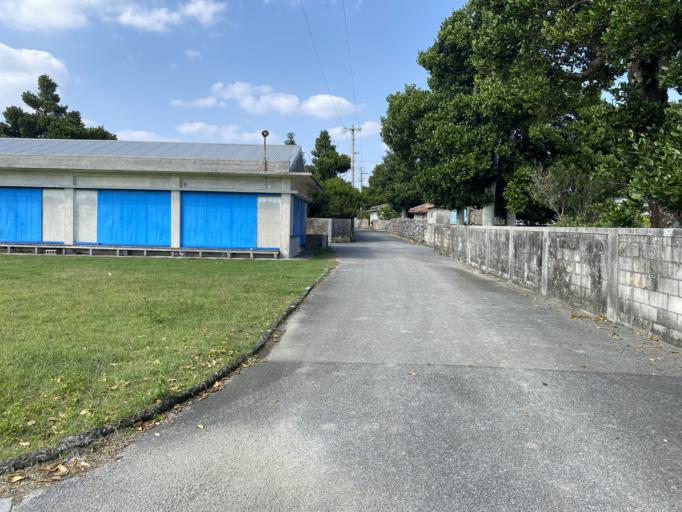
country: JP
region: Okinawa
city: Ishigaki
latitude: 24.0594
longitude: 123.7763
